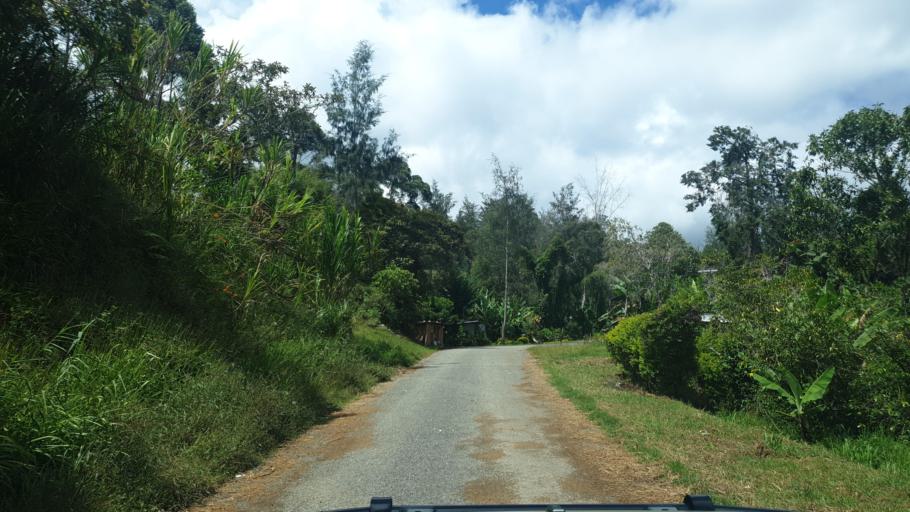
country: PG
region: Chimbu
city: Kundiawa
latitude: -6.1565
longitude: 145.1344
